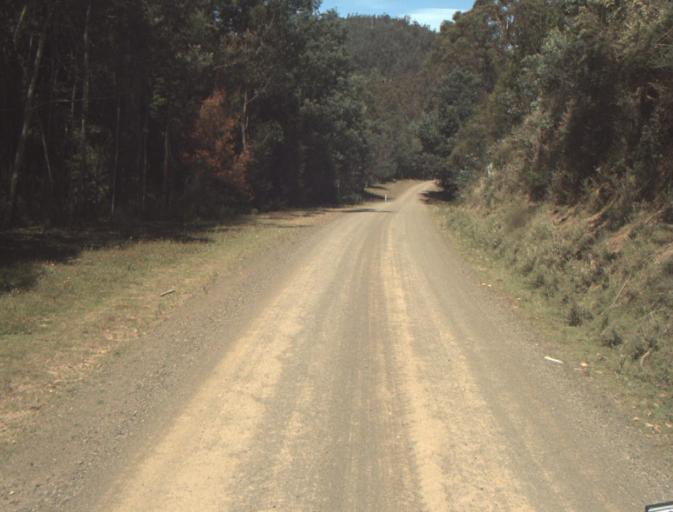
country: AU
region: Tasmania
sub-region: Dorset
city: Scottsdale
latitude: -41.3748
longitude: 147.4750
